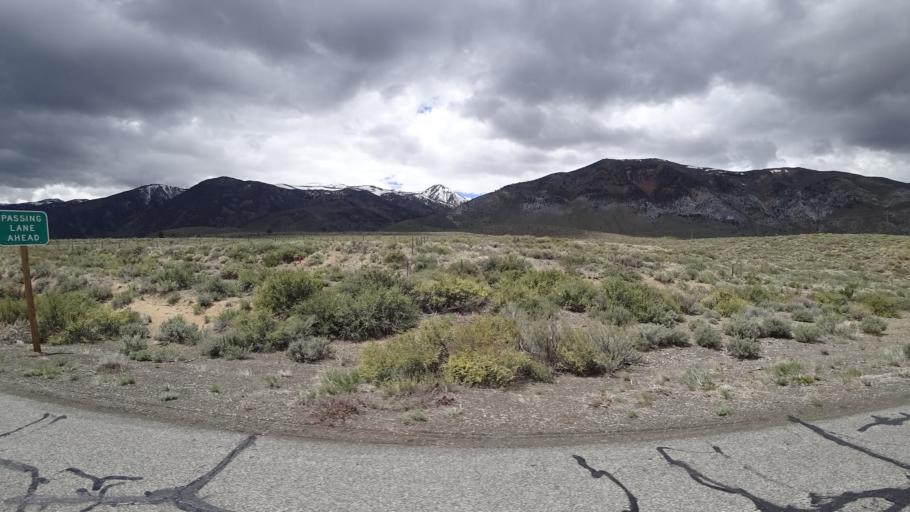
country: US
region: California
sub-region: Mono County
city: Bridgeport
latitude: 38.0441
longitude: -119.1601
